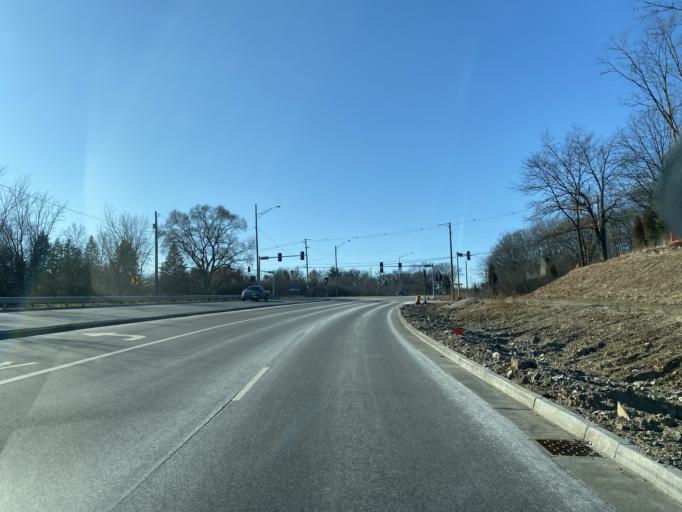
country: US
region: Illinois
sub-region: Will County
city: Goodings Grove
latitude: 41.6855
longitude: -87.9319
